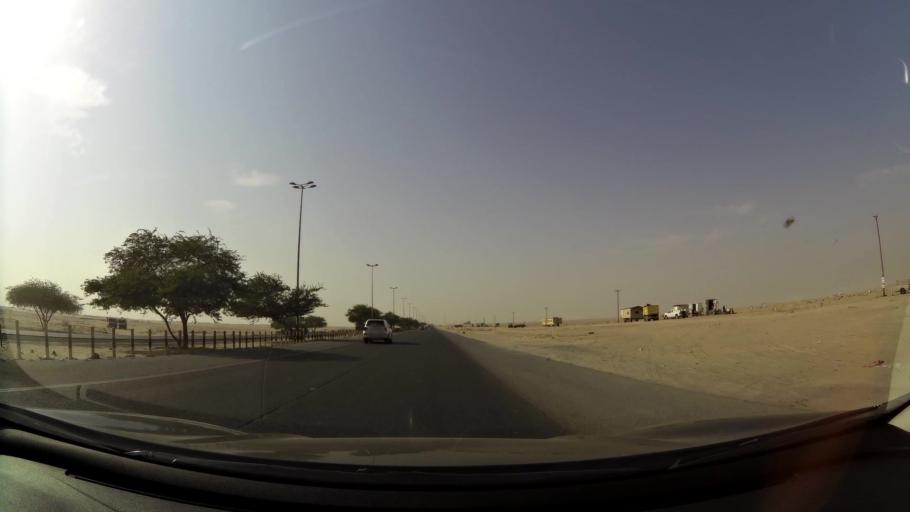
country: KW
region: Al Ahmadi
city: Al Ahmadi
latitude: 28.9225
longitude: 48.1026
